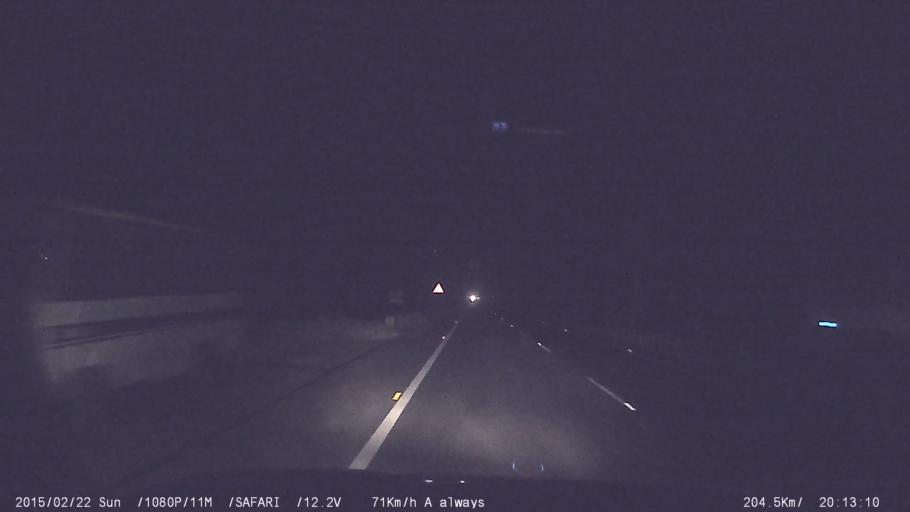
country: IN
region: Tamil Nadu
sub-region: Dindigul
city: Nilakottai
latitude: 10.2443
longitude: 77.8239
